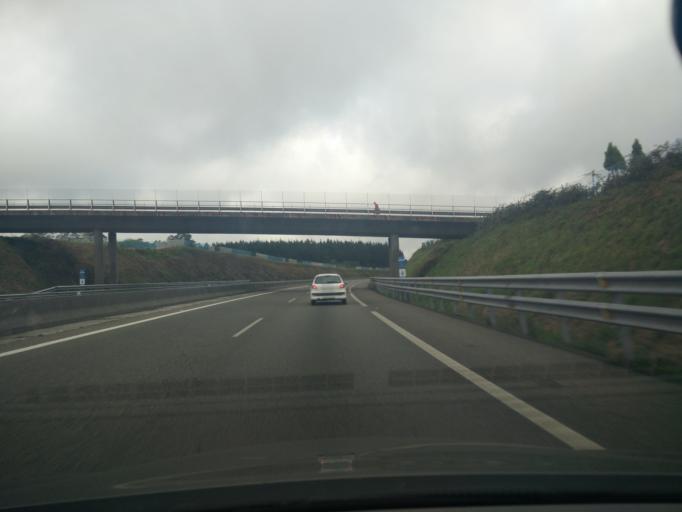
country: ES
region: Galicia
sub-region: Provincia da Coruna
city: Laracha
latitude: 43.2708
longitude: -8.5790
